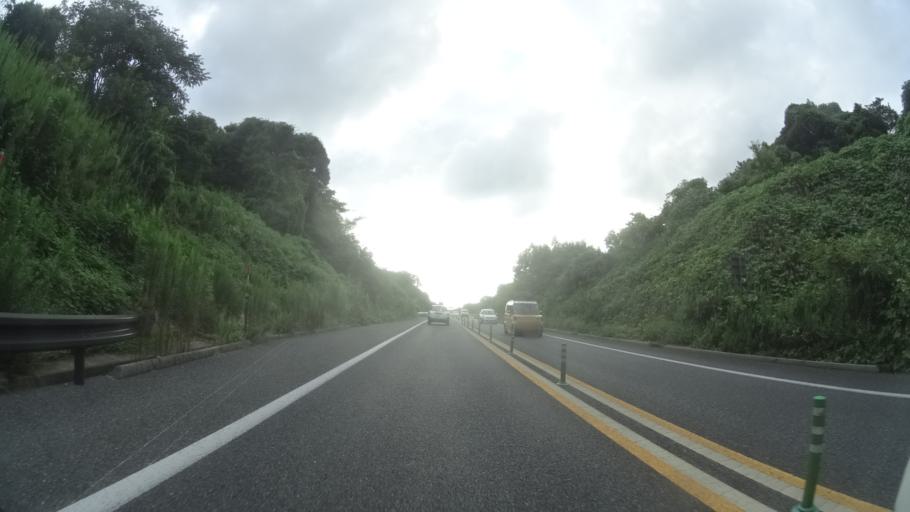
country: JP
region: Tottori
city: Kurayoshi
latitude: 35.5076
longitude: 133.6094
